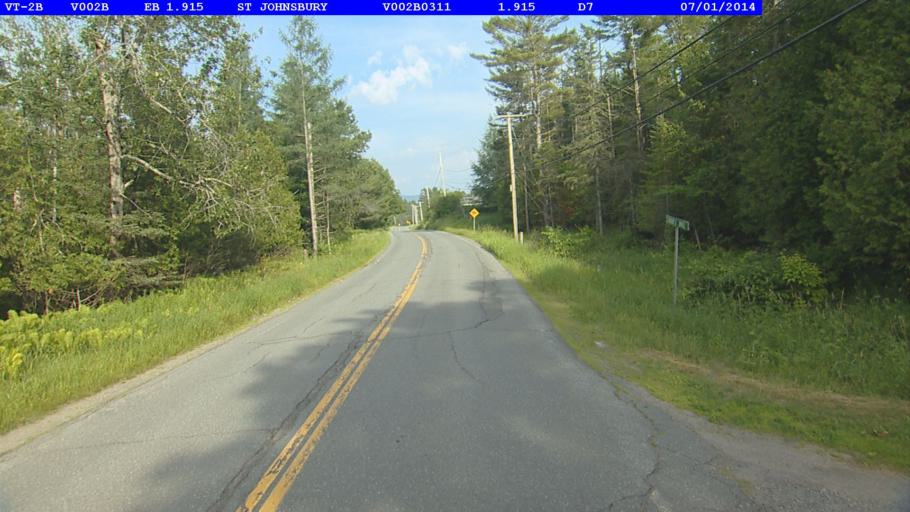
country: US
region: Vermont
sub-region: Caledonia County
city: St Johnsbury
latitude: 44.4294
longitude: -72.0560
